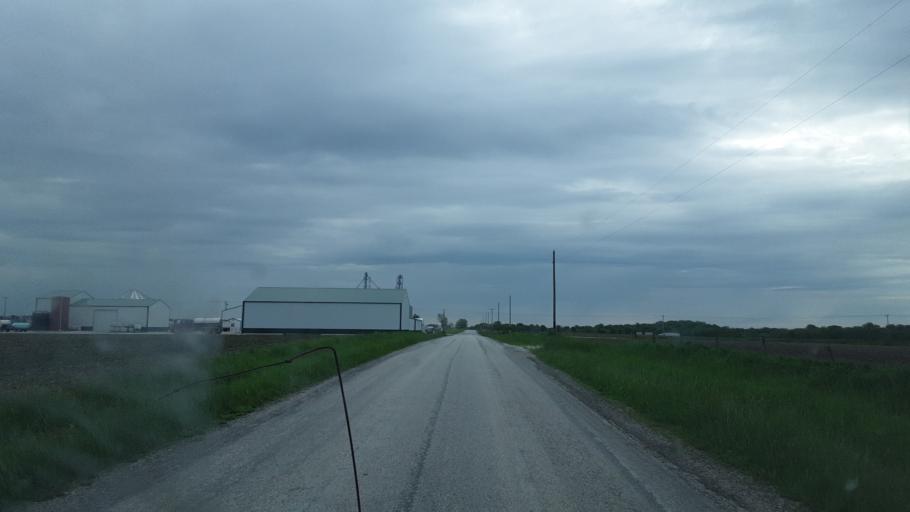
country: US
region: Illinois
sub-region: McDonough County
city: Macomb
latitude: 40.3816
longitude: -90.6225
